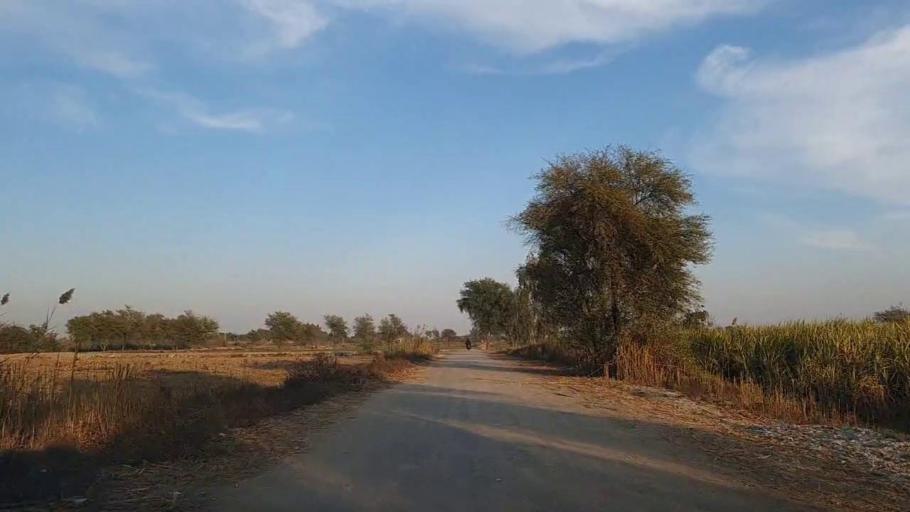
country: PK
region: Sindh
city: Bandhi
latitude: 26.5974
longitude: 68.3465
